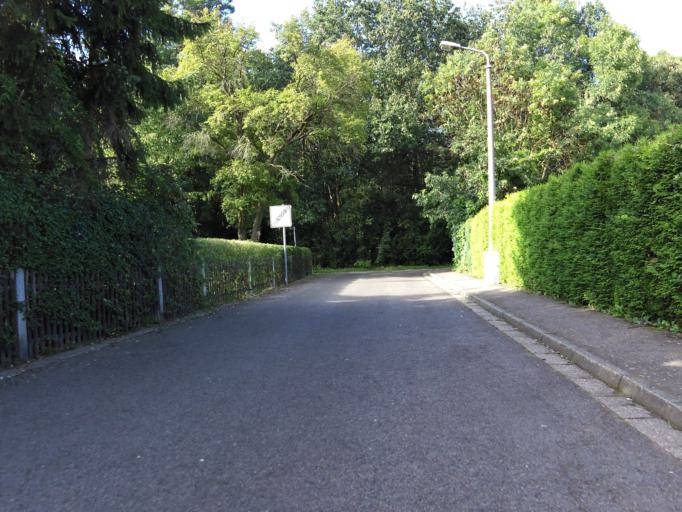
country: DE
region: Saxony
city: Markkleeberg
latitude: 51.2942
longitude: 12.4217
